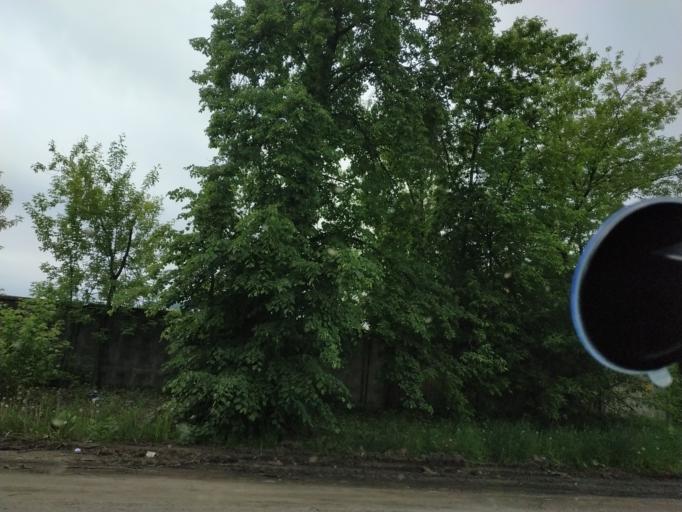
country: RU
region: Moskovskaya
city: Zhukovskiy
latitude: 55.5587
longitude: 38.1113
